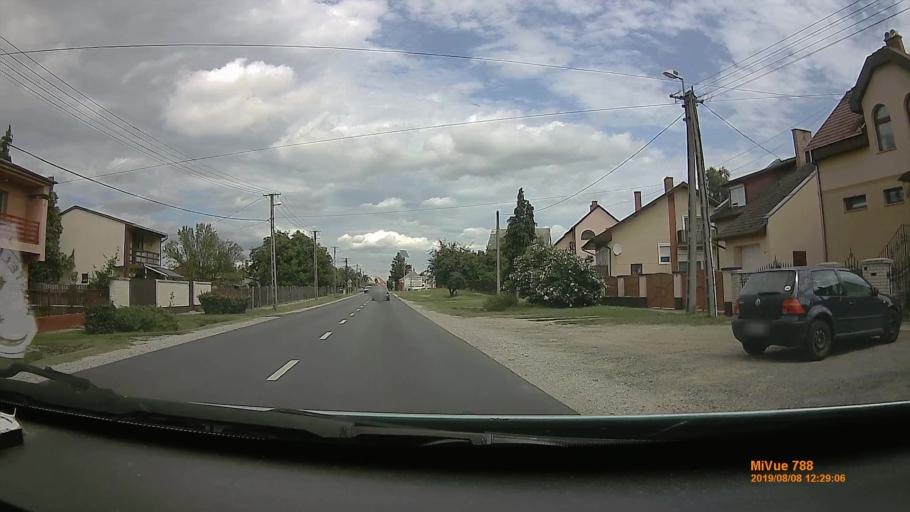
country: HU
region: Szabolcs-Szatmar-Bereg
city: Nyirbator
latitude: 47.8333
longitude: 22.1168
